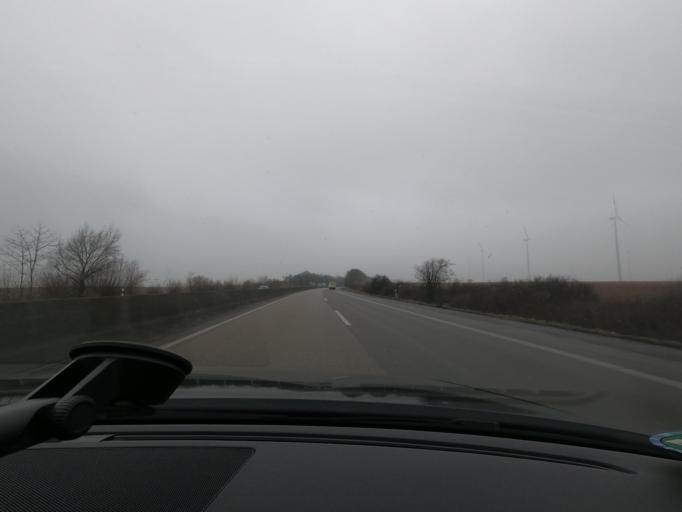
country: DE
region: North Rhine-Westphalia
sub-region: Regierungsbezirk Koln
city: Titz
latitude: 51.0165
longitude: 6.4908
